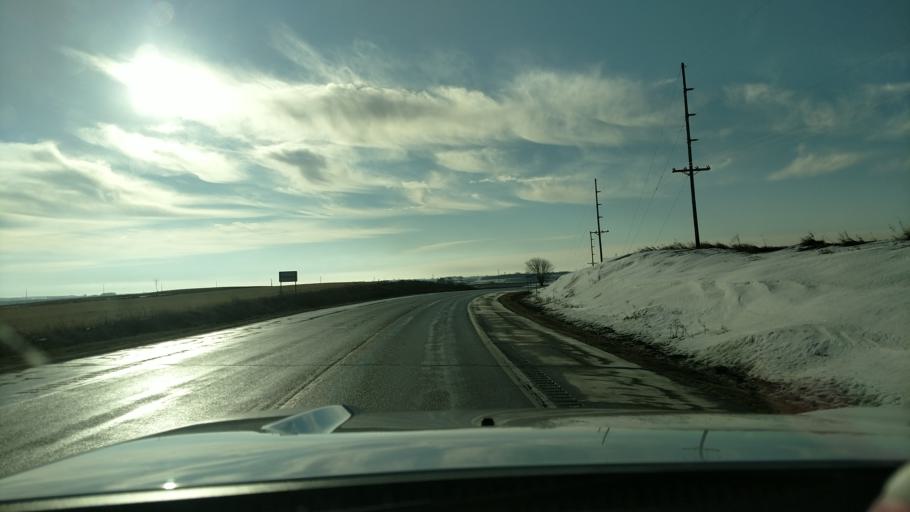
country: US
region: Minnesota
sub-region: Olmsted County
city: Oronoco
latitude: 44.1940
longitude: -92.4212
